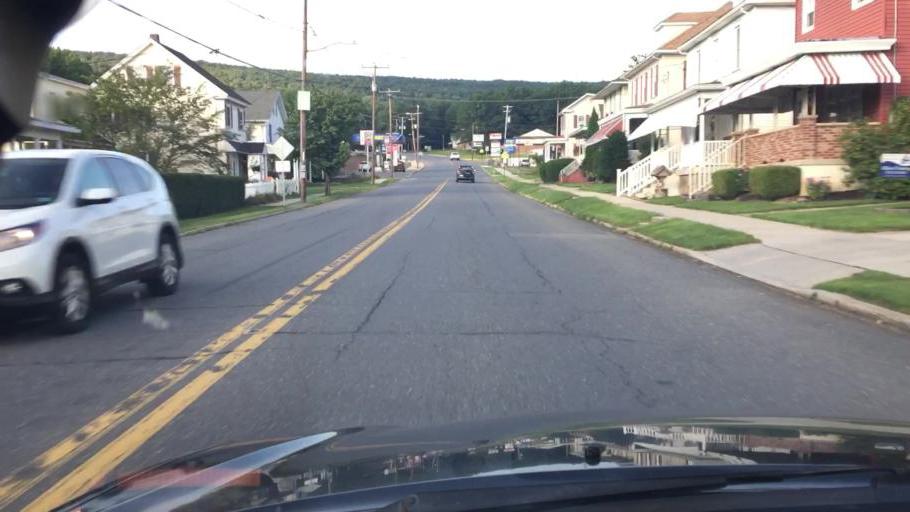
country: US
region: Pennsylvania
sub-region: Carbon County
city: Jim Thorpe
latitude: 40.8799
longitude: -75.7280
